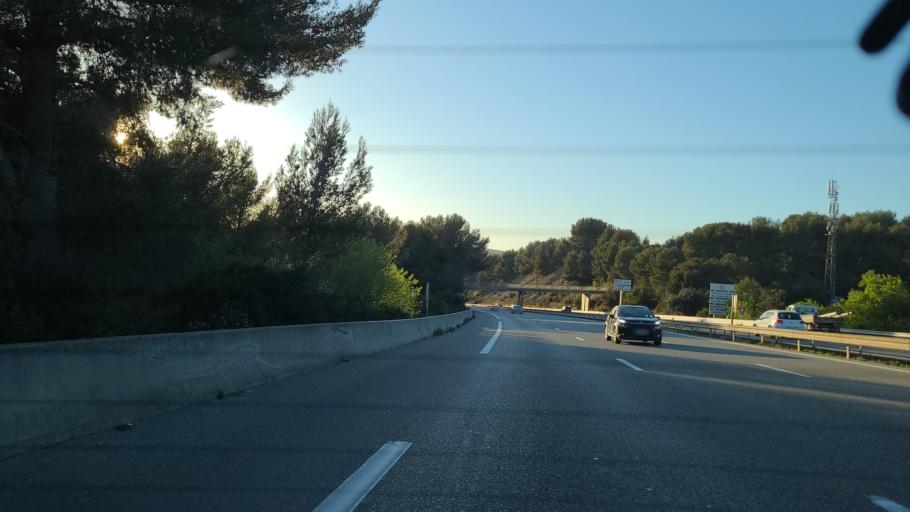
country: FR
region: Provence-Alpes-Cote d'Azur
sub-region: Departement du Var
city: Sanary-sur-Mer
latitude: 43.1451
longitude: 5.7845
